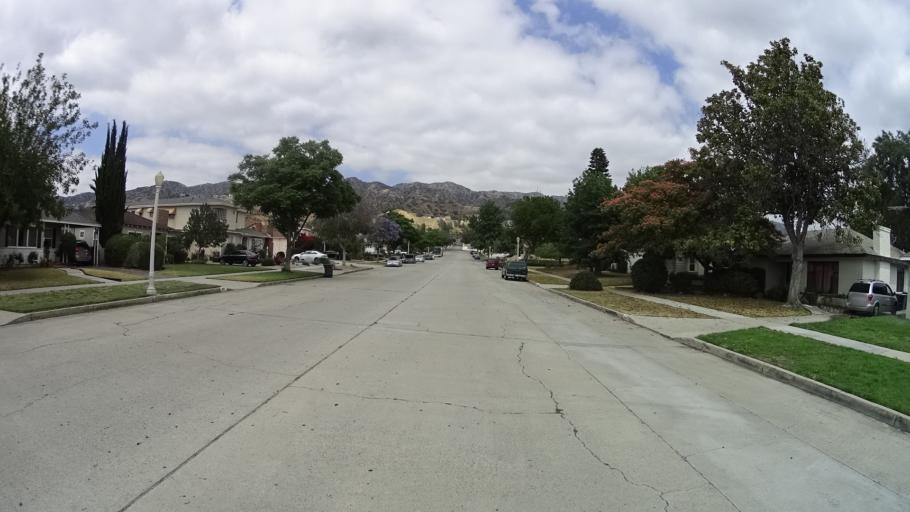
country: US
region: California
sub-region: Los Angeles County
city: Burbank
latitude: 34.1971
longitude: -118.3242
